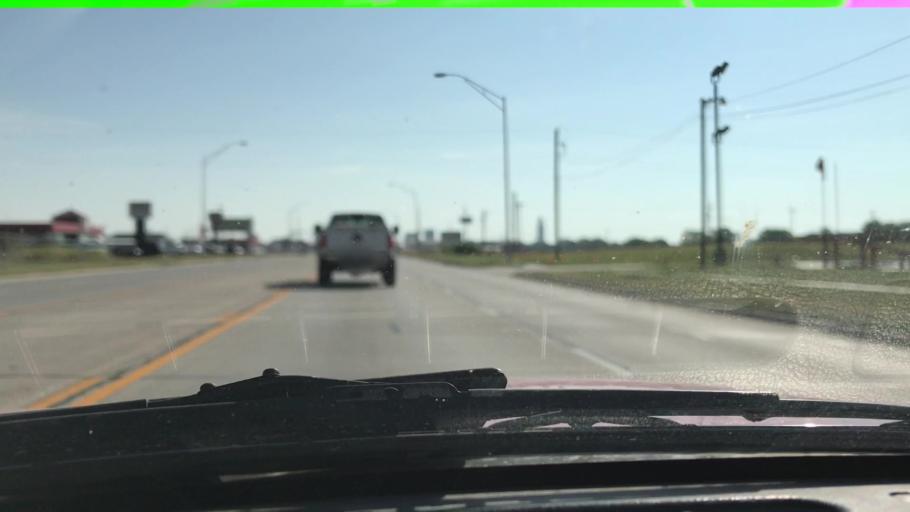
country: US
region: Nebraska
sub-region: Lancaster County
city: Lincoln
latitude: 40.8137
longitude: -96.7354
